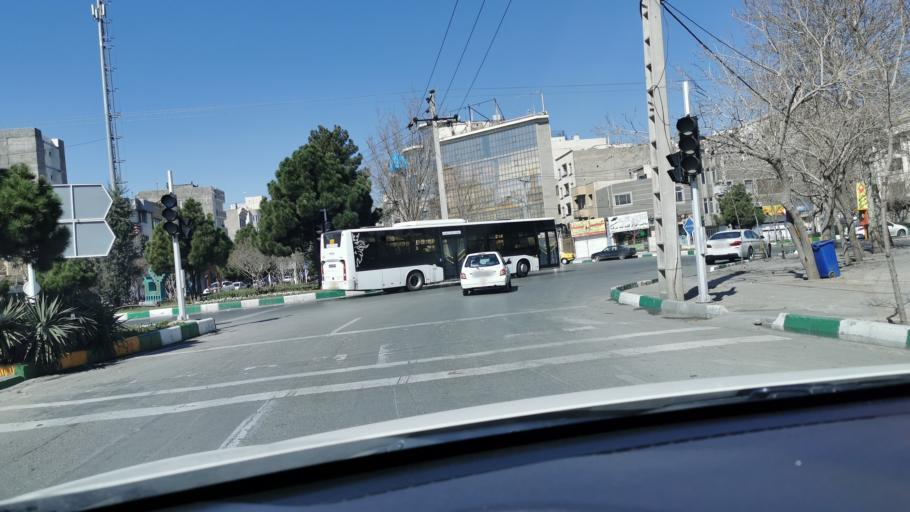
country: IR
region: Razavi Khorasan
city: Mashhad
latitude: 36.3269
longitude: 59.5187
